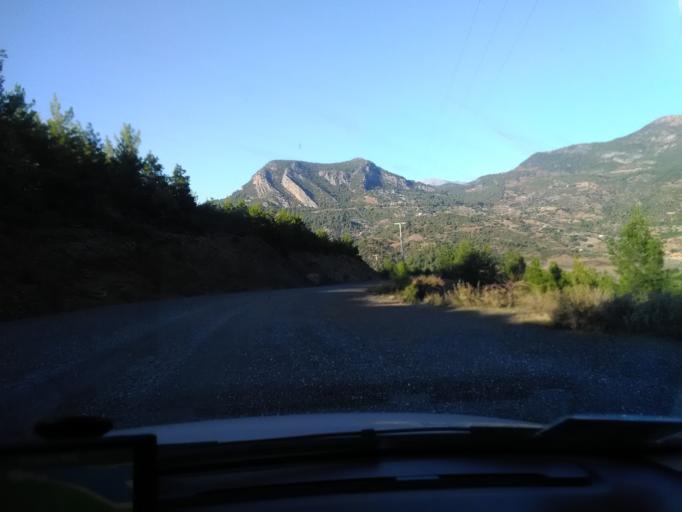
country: TR
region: Antalya
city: Gazipasa
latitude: 36.3068
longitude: 32.3985
